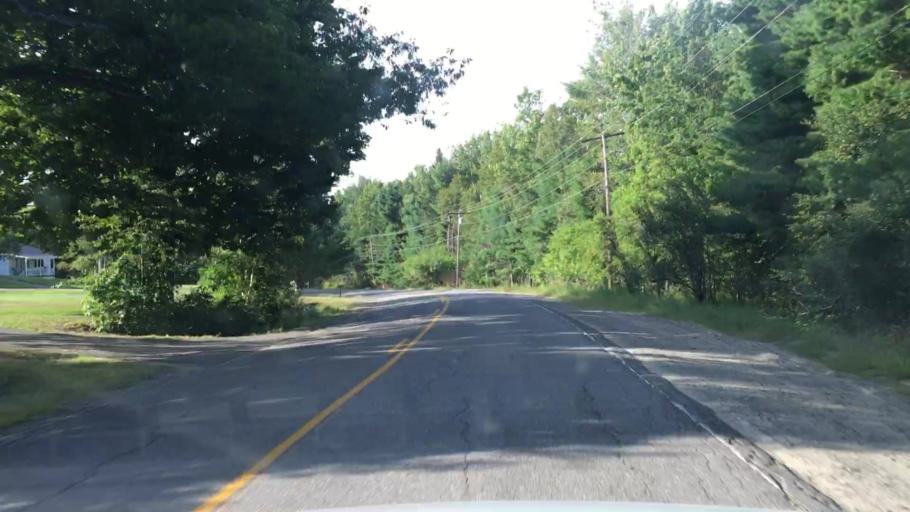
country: US
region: Maine
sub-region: Penobscot County
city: Enfield
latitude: 45.2351
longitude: -68.5441
